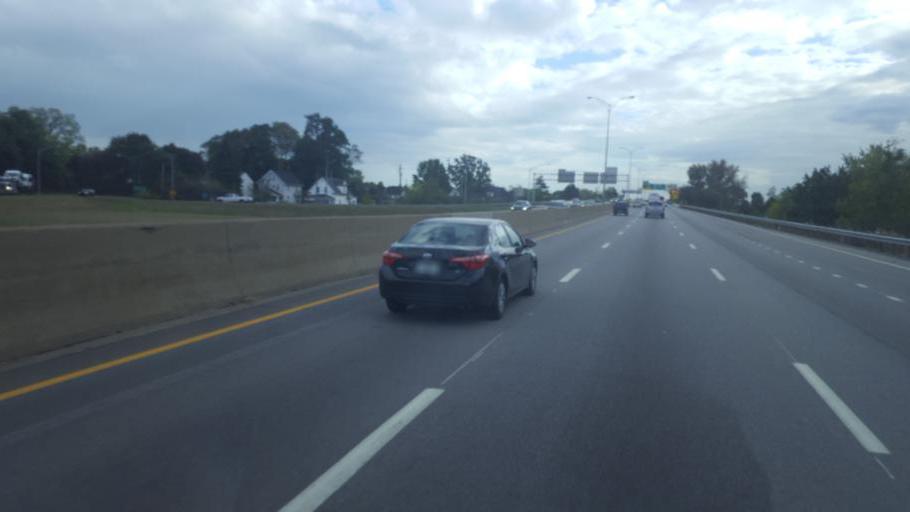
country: US
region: Ohio
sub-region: Summit County
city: Barberton
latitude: 41.0435
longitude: -81.5652
